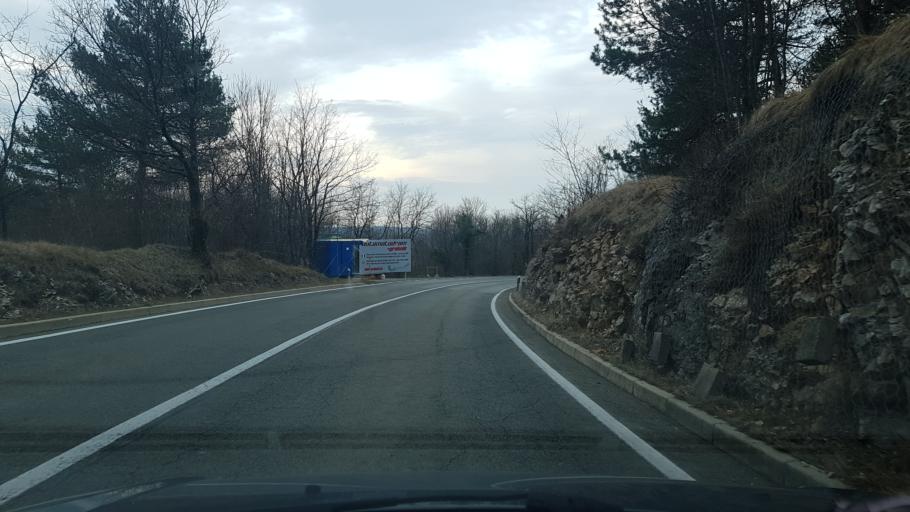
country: SI
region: Ilirska Bistrica
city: Ilirska Bistrica
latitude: 45.4872
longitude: 14.2303
